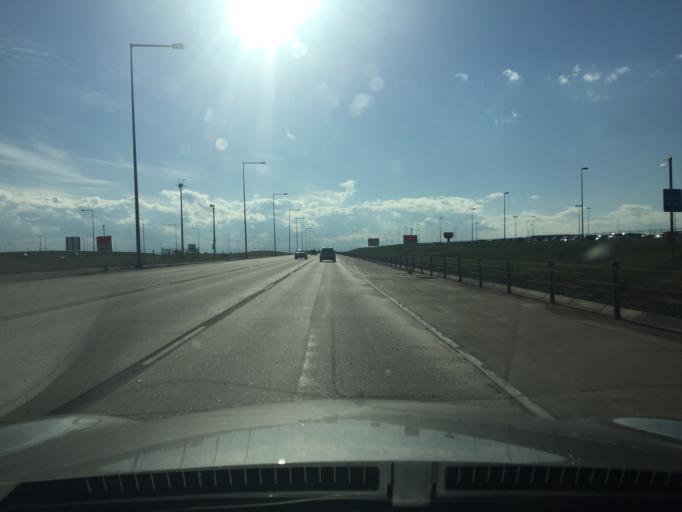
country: US
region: Colorado
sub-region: Adams County
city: Aurora
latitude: 39.8344
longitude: -104.7035
